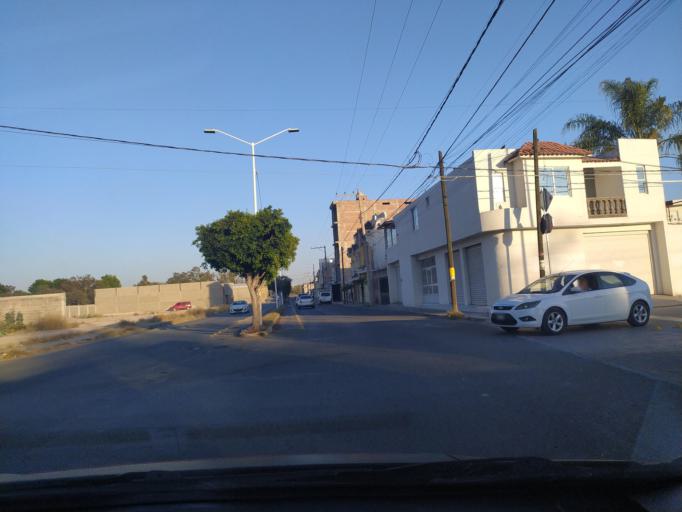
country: MX
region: Guanajuato
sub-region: San Francisco del Rincon
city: Fraccionamiento la Mezquitera
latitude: 21.0121
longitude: -101.8393
